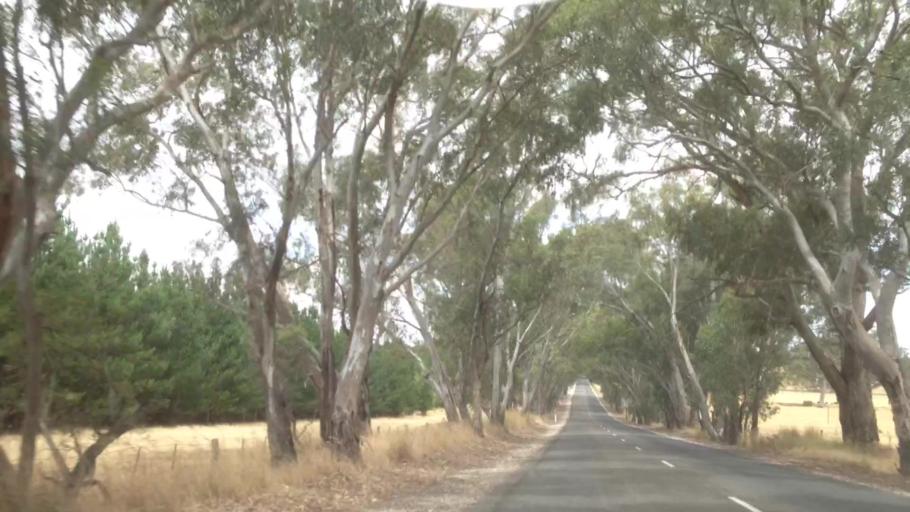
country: AU
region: South Australia
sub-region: Barossa
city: Williamstown
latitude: -34.6875
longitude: 138.9801
